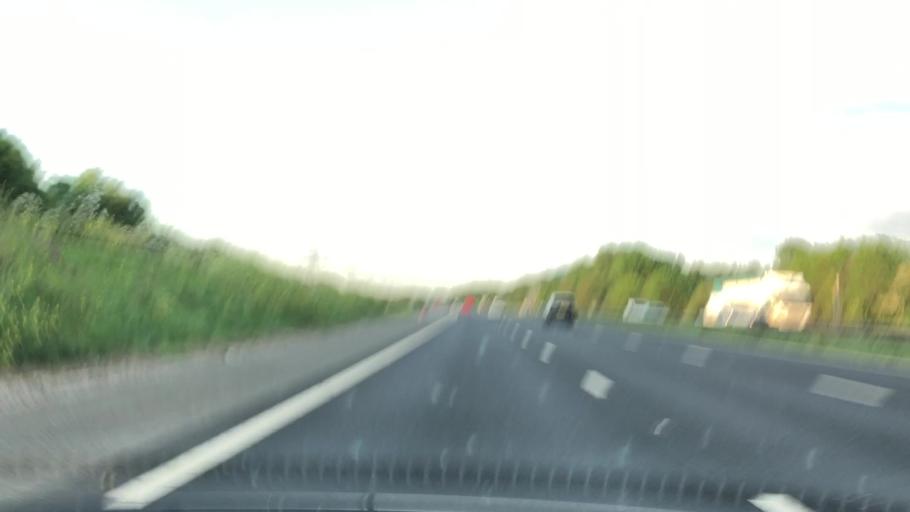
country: GB
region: England
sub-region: Cheshire West and Chester
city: Elton
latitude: 53.2674
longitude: -2.8006
